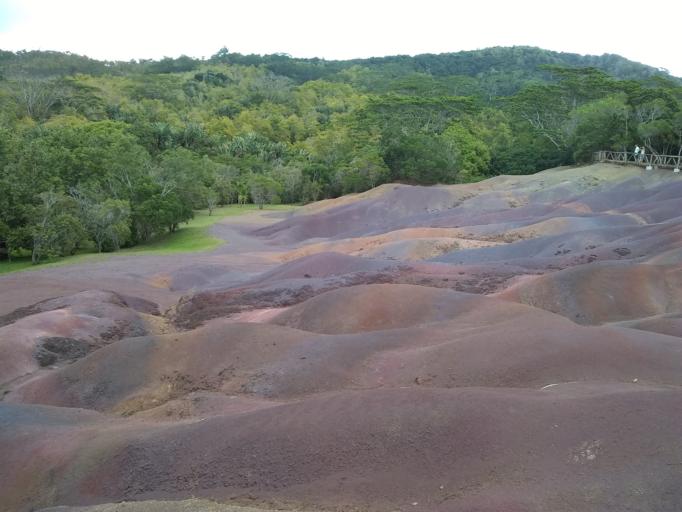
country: MU
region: Black River
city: Petite Case Noyale
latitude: -20.4406
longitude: 57.3736
